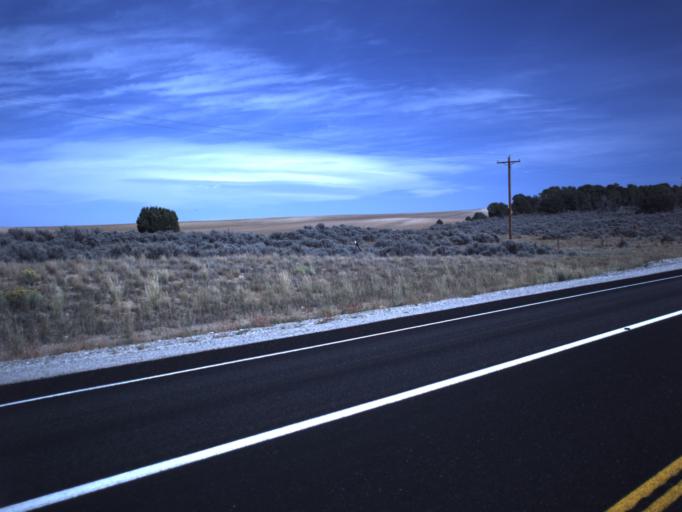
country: US
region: Utah
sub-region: San Juan County
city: Monticello
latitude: 37.8432
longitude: -109.1352
